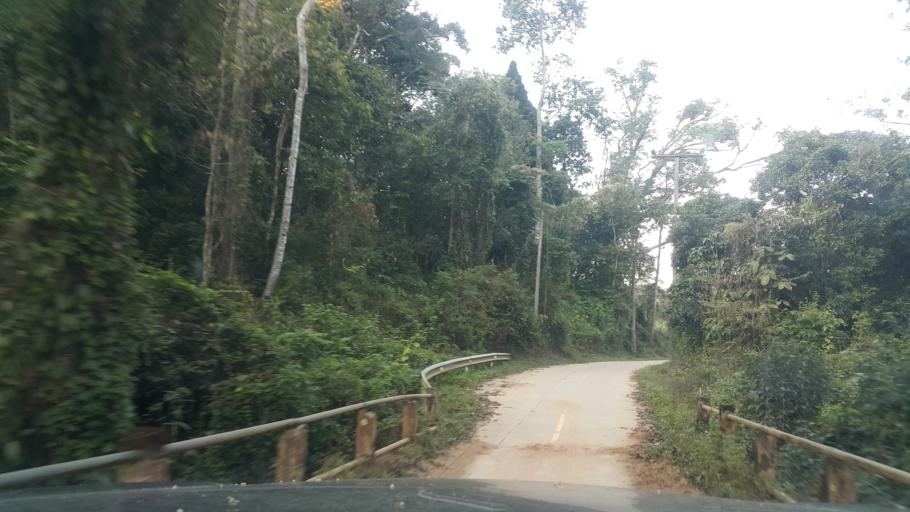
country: TH
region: Chiang Mai
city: Samoeng
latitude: 19.0070
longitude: 98.6721
